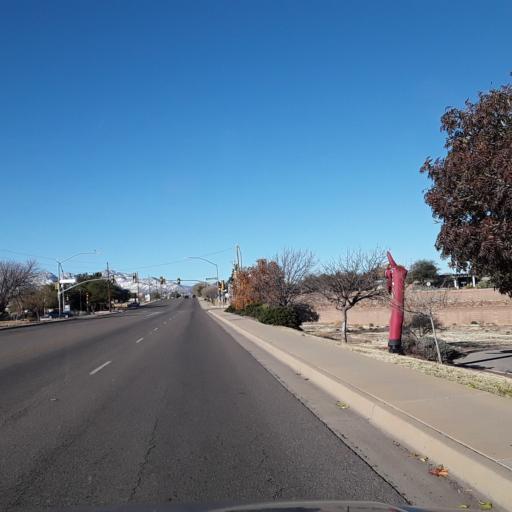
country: US
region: Arizona
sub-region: Cochise County
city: Sierra Vista
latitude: 31.5547
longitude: -110.2604
